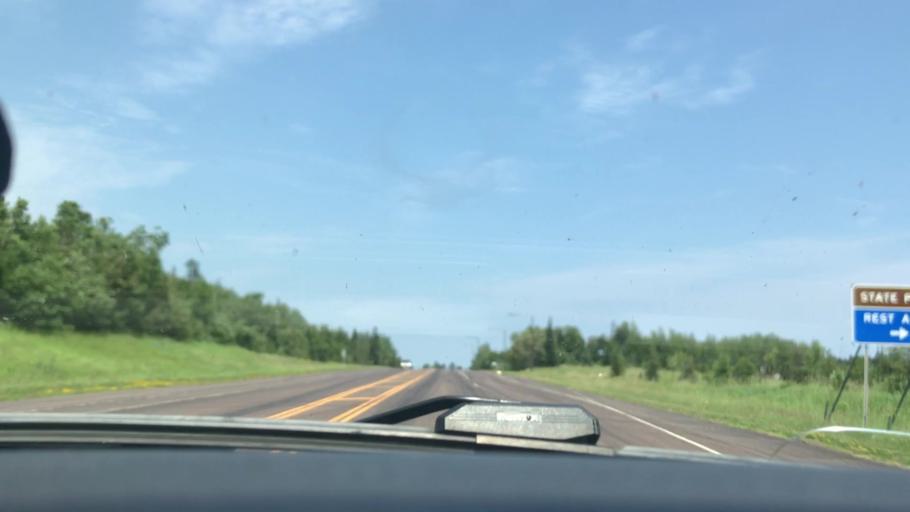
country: US
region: Minnesota
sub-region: Lake County
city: Silver Bay
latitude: 47.3386
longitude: -91.1986
